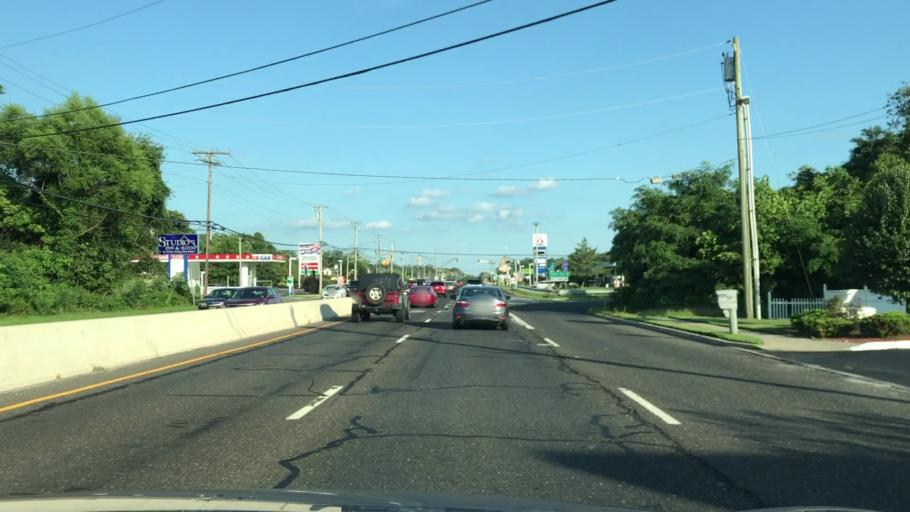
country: US
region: New Jersey
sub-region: Atlantic County
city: Absecon
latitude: 39.4453
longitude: -74.5274
